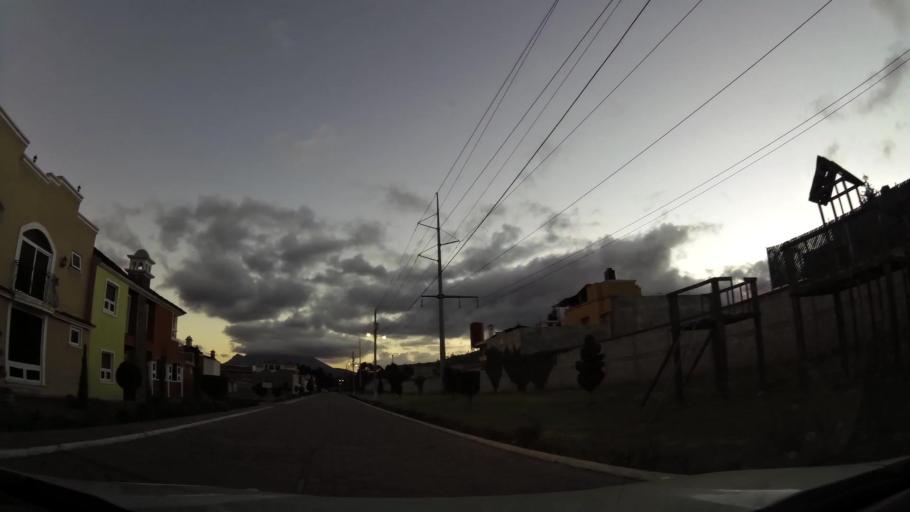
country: GT
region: Quetzaltenango
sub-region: Municipio de La Esperanza
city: La Esperanza
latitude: 14.8634
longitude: -91.5452
